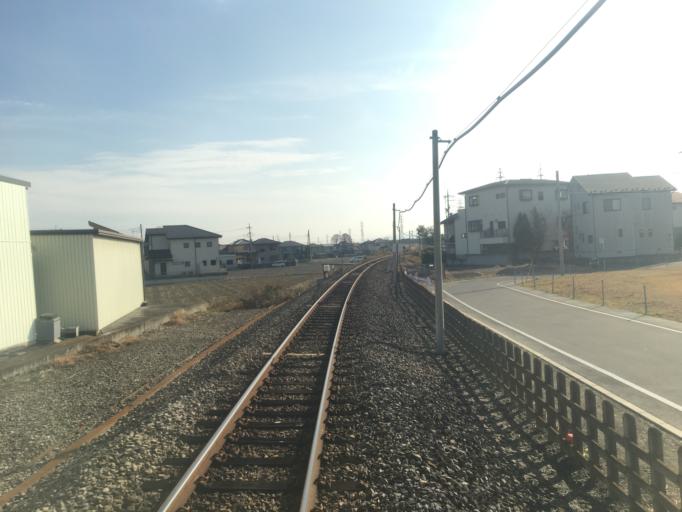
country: JP
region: Gunma
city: Fujioka
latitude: 36.2801
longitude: 139.0833
